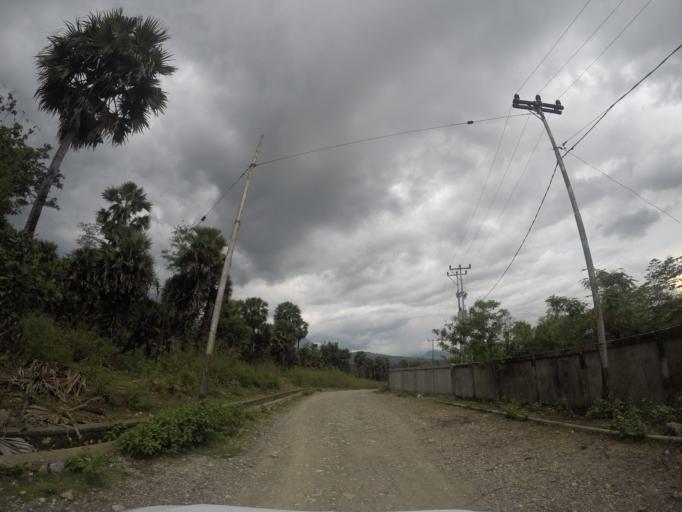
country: TL
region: Bobonaro
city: Maliana
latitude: -8.9722
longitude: 125.2269
